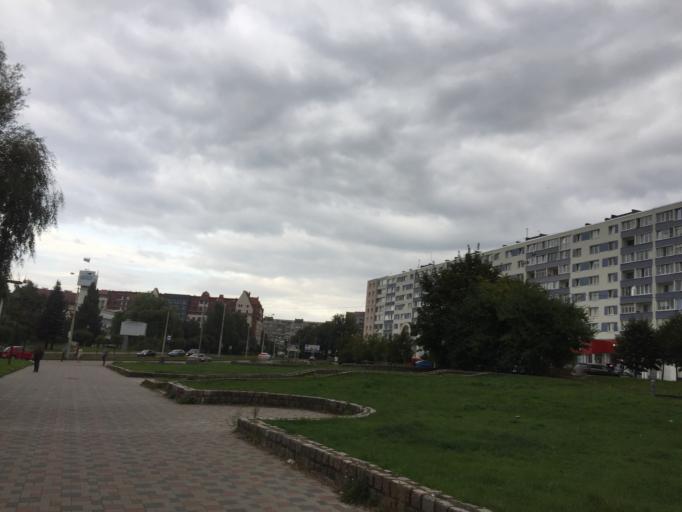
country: RU
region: Kaliningrad
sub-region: Gorod Kaliningrad
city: Kaliningrad
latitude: 54.7100
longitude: 20.5158
